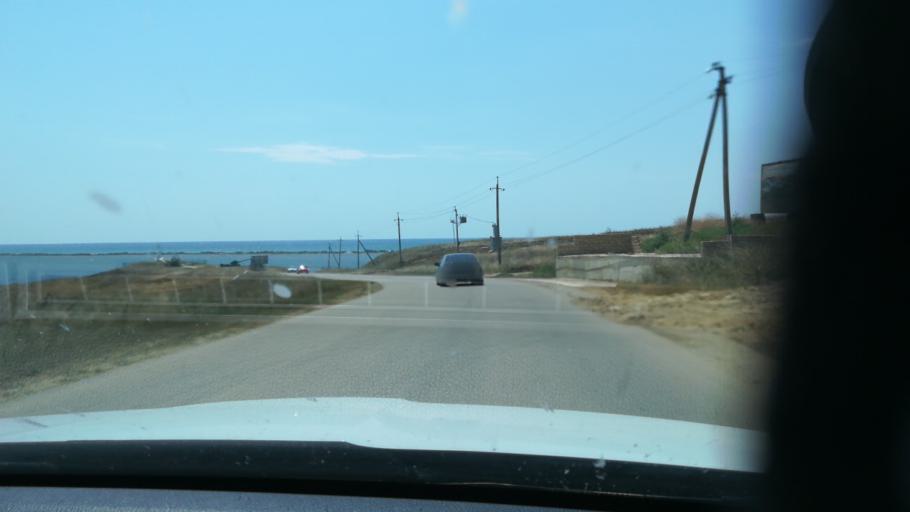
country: RU
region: Krasnodarskiy
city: Vyshestebliyevskaya
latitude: 45.1200
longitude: 36.8948
